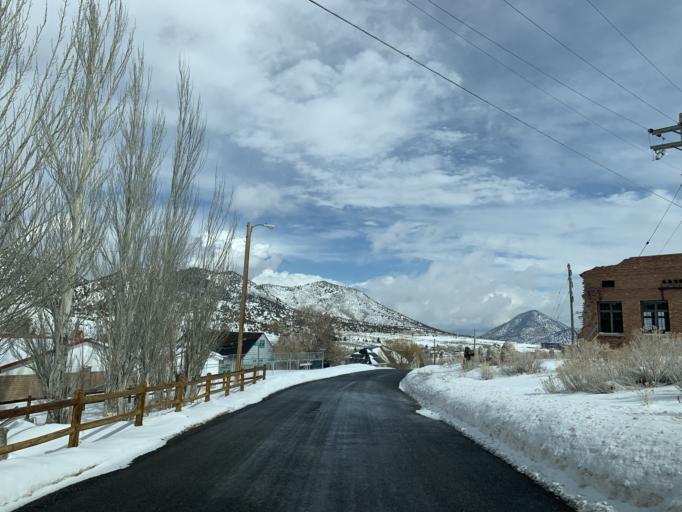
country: US
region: Utah
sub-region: Utah County
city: Genola
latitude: 39.9512
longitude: -112.1145
